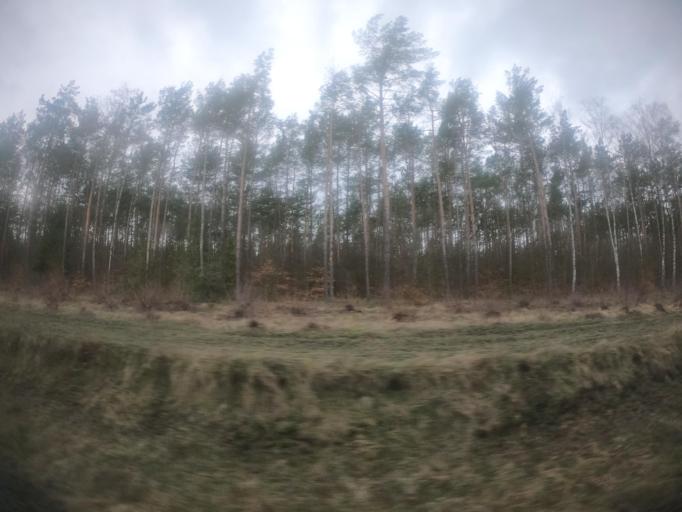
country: PL
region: West Pomeranian Voivodeship
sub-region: Powiat szczecinecki
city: Bialy Bor
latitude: 53.7872
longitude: 16.8597
